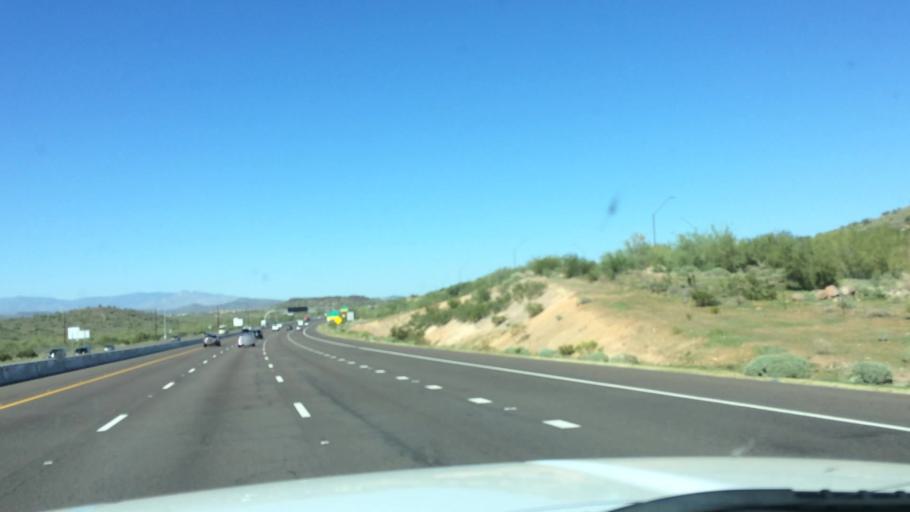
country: US
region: Arizona
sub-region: Maricopa County
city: Anthem
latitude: 33.8276
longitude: -112.1431
